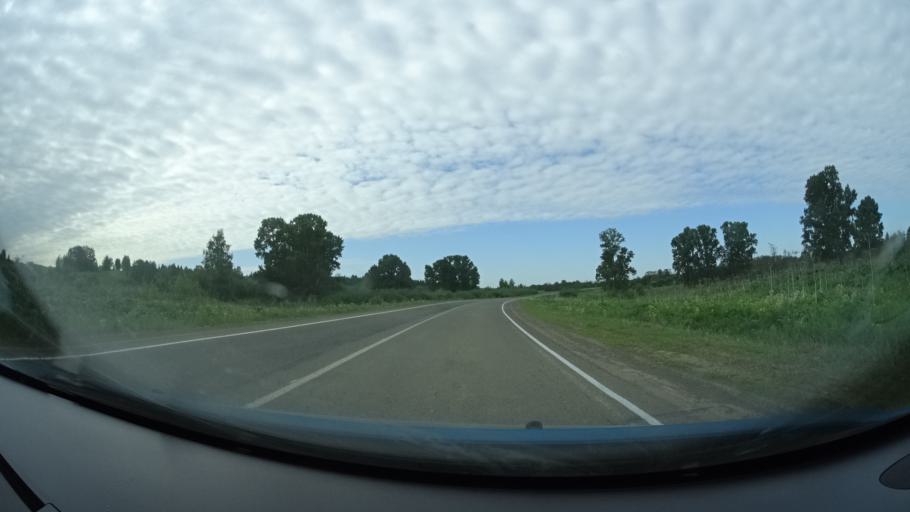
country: RU
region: Perm
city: Kuyeda
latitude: 56.5071
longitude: 55.6269
